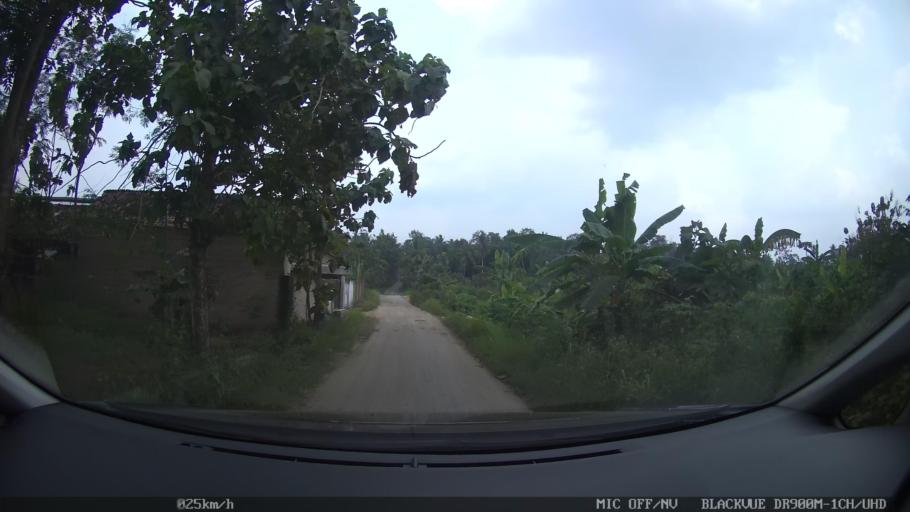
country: ID
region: Lampung
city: Gadingrejo
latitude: -5.3884
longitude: 105.0358
